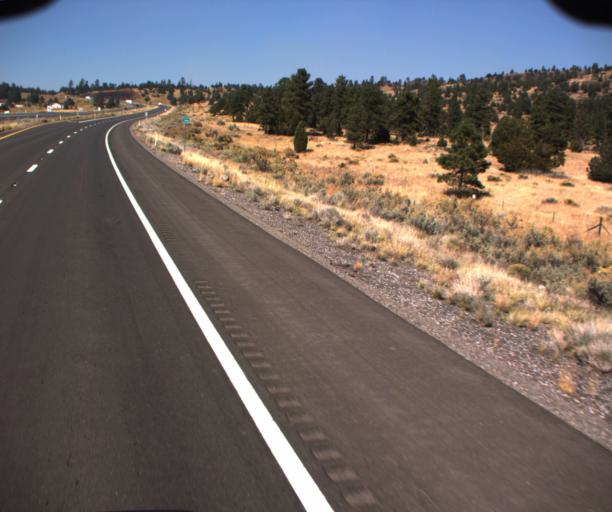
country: US
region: Arizona
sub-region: Coconino County
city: Flagstaff
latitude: 35.3428
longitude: -111.5599
